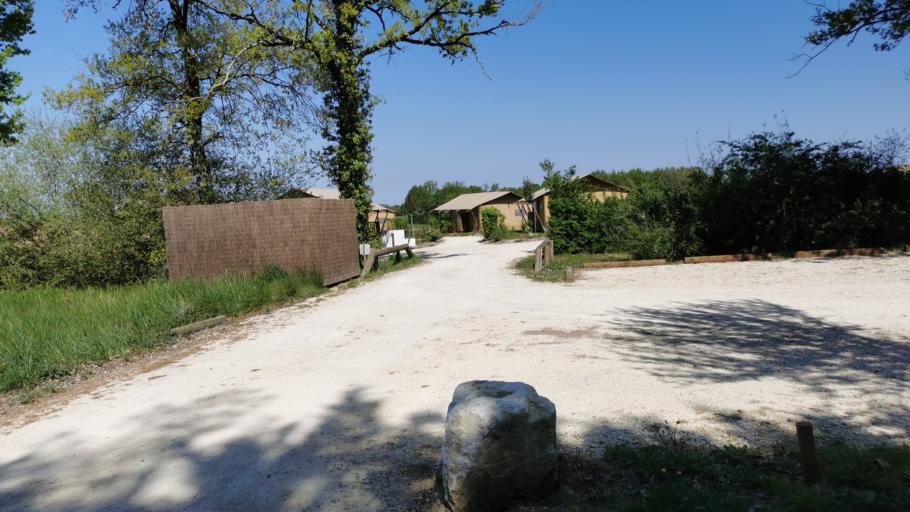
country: FR
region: Poitou-Charentes
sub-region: Departement de la Vienne
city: Availles-Limouzine
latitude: 46.1253
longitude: 0.5496
